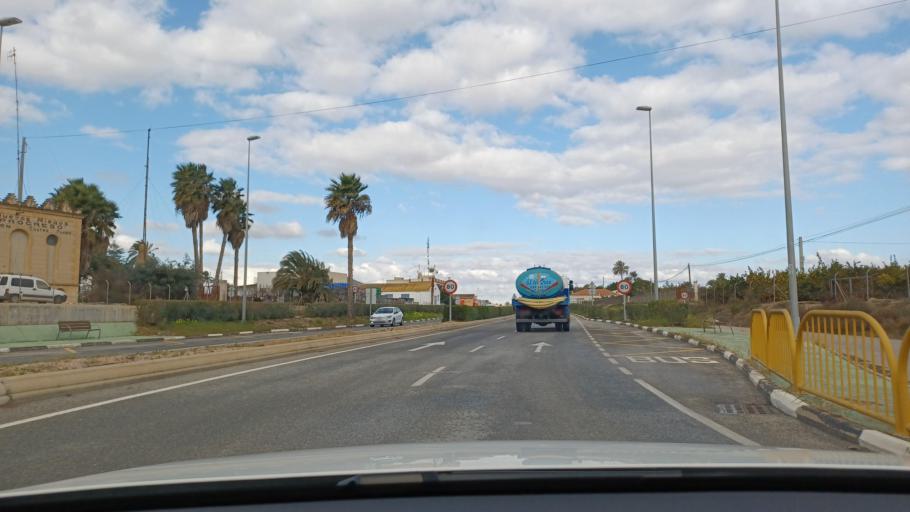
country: ES
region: Valencia
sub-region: Provincia de Alicante
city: Elche
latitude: 38.2220
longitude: -0.6978
